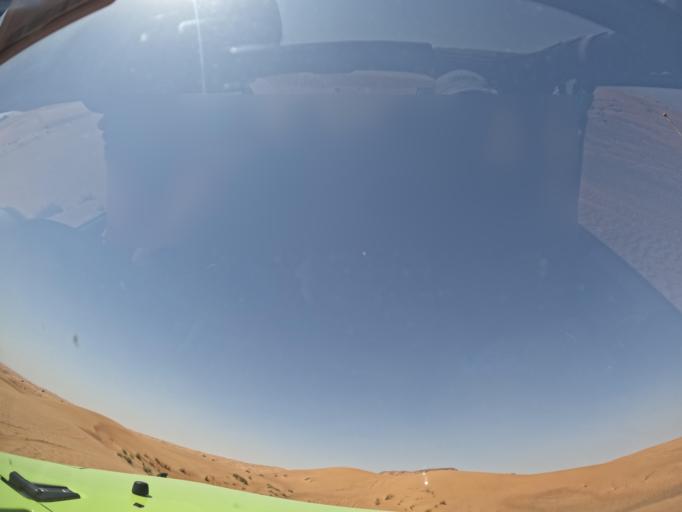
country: AE
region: Ash Shariqah
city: Adh Dhayd
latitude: 25.0192
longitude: 55.7425
